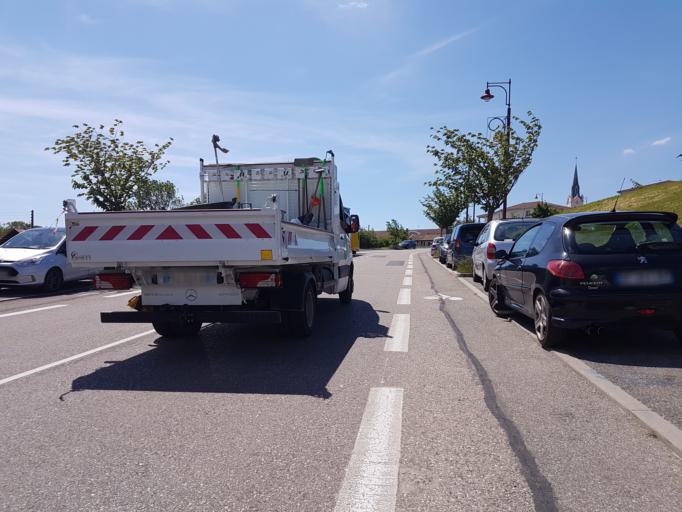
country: FR
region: Rhone-Alpes
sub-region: Departement du Rhone
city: Jonage
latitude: 45.7956
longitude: 5.0496
